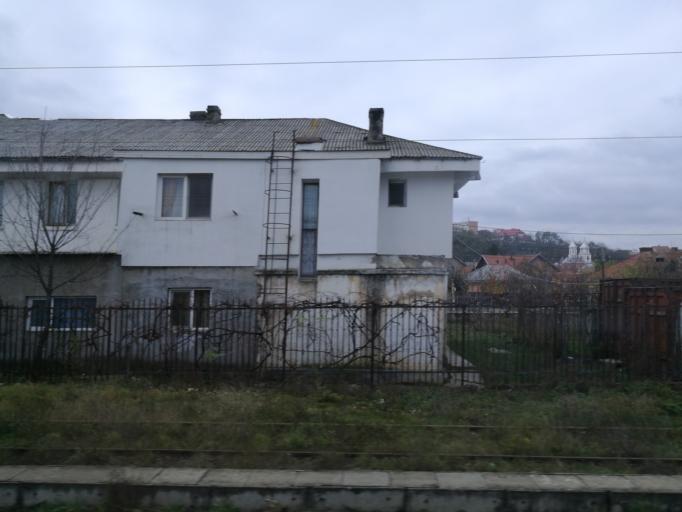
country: RO
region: Iasi
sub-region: Municipiul Pascani
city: Pascani
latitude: 47.2512
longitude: 26.7276
